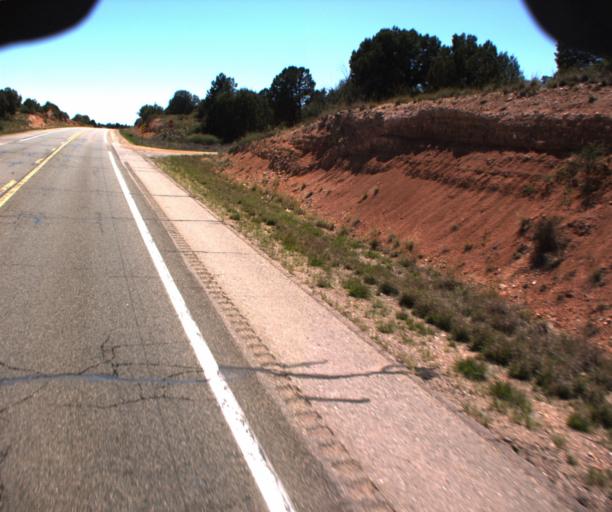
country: US
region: Arizona
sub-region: Yavapai County
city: Paulden
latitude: 34.9744
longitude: -112.4051
